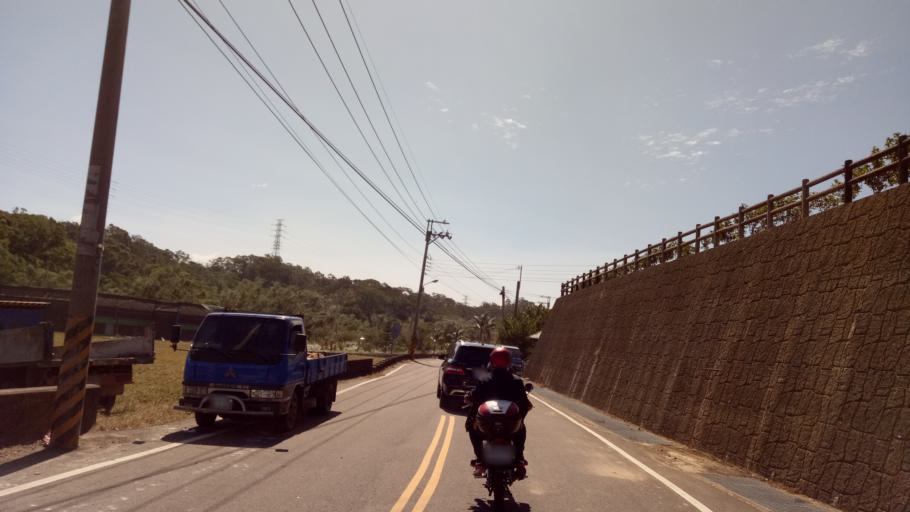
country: TW
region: Taiwan
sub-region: Hsinchu
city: Hsinchu
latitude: 24.7372
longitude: 120.9484
